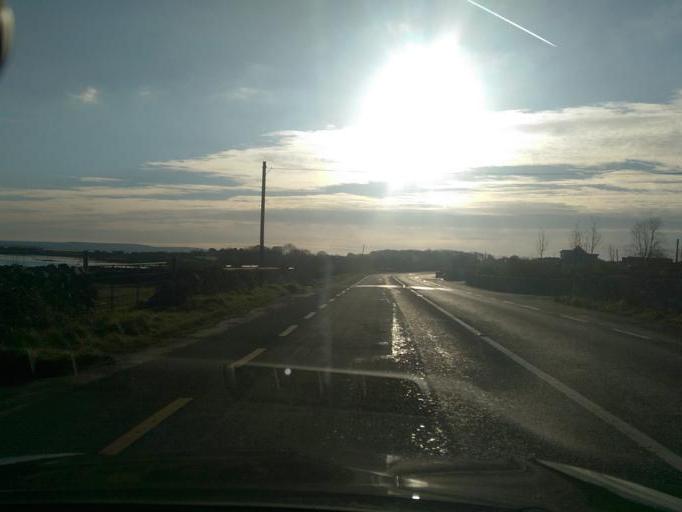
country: IE
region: Connaught
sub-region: County Galway
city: Oranmore
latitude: 53.2724
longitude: -8.9674
